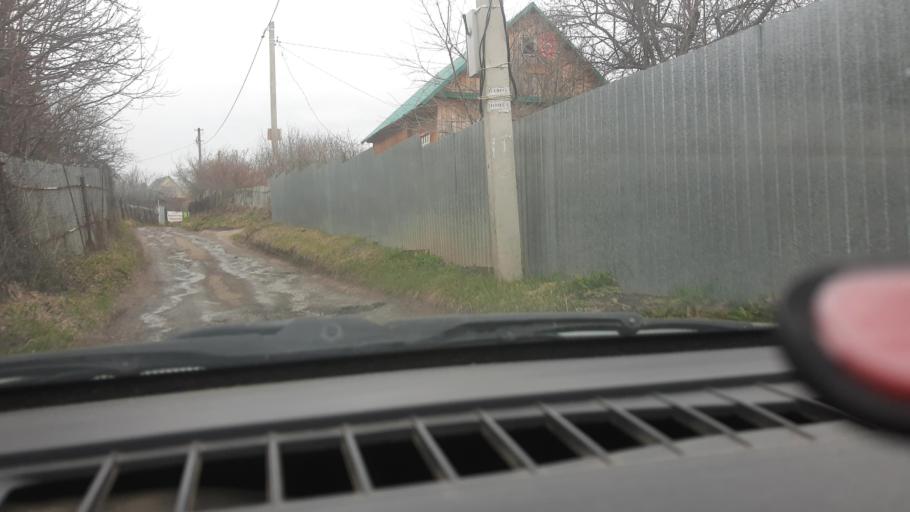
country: RU
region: Bashkortostan
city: Mikhaylovka
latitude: 54.9215
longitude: 55.8839
